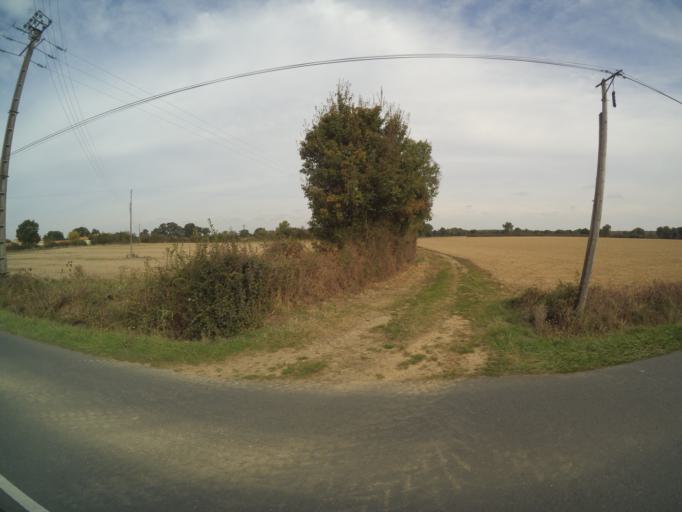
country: FR
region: Pays de la Loire
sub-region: Departement de Maine-et-Loire
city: Melay
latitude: 47.2068
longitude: -0.6626
